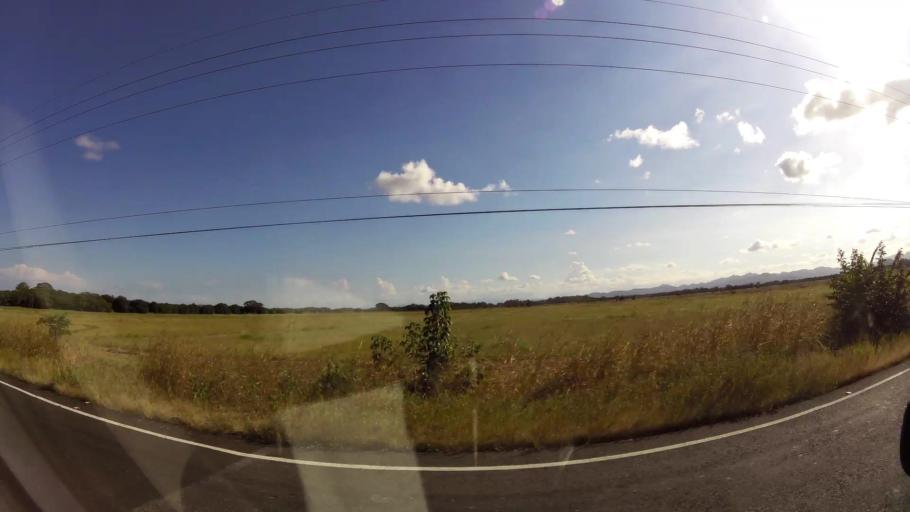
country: CR
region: Guanacaste
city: Sardinal
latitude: 10.5661
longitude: -85.6044
